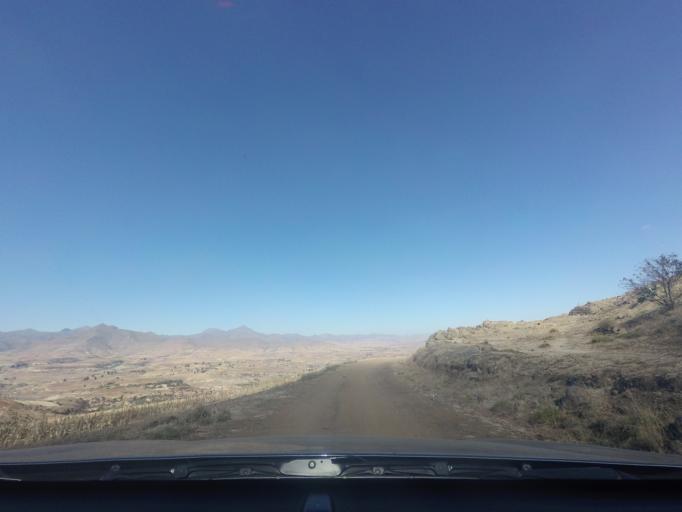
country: LS
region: Berea
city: Teyateyaneng
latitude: -29.2368
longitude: 27.8706
